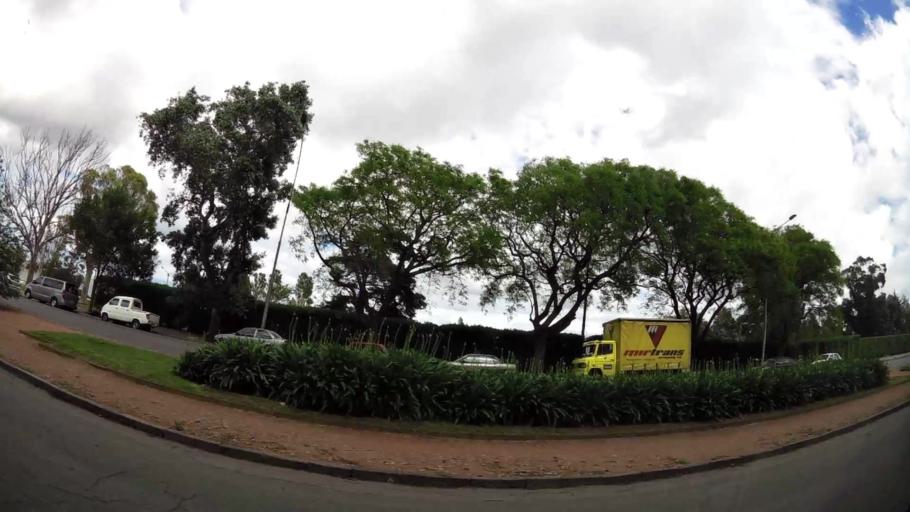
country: UY
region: Montevideo
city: Montevideo
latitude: -34.9272
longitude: -56.1614
